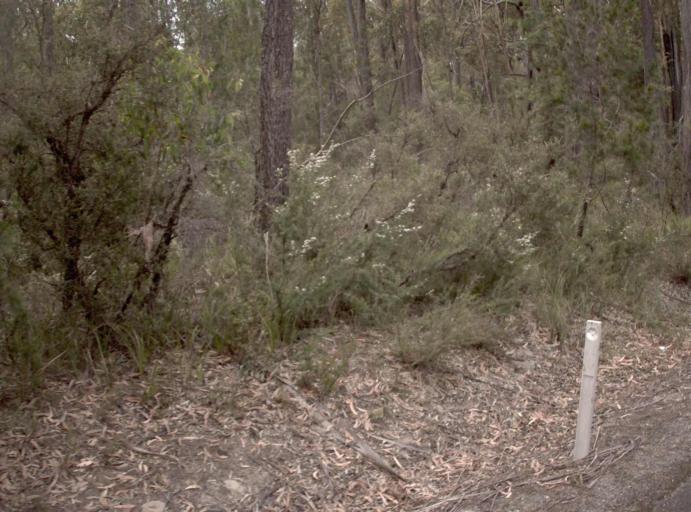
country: AU
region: New South Wales
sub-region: Bega Valley
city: Eden
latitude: -37.4940
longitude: 149.5494
